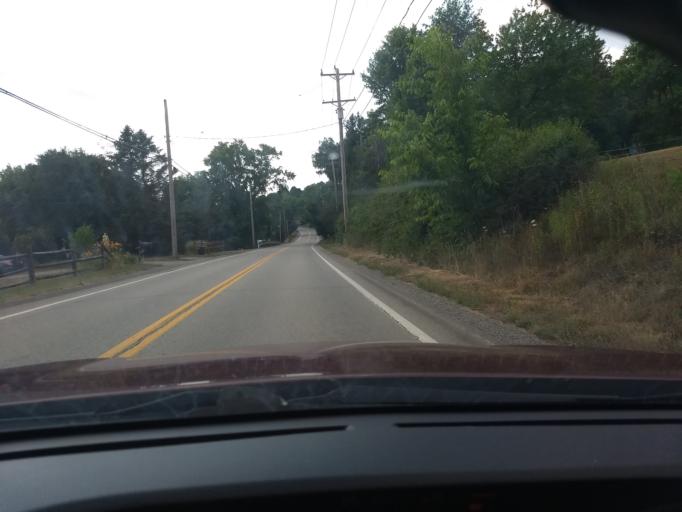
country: US
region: Pennsylvania
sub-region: Allegheny County
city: Curtisville
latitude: 40.6304
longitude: -79.8656
